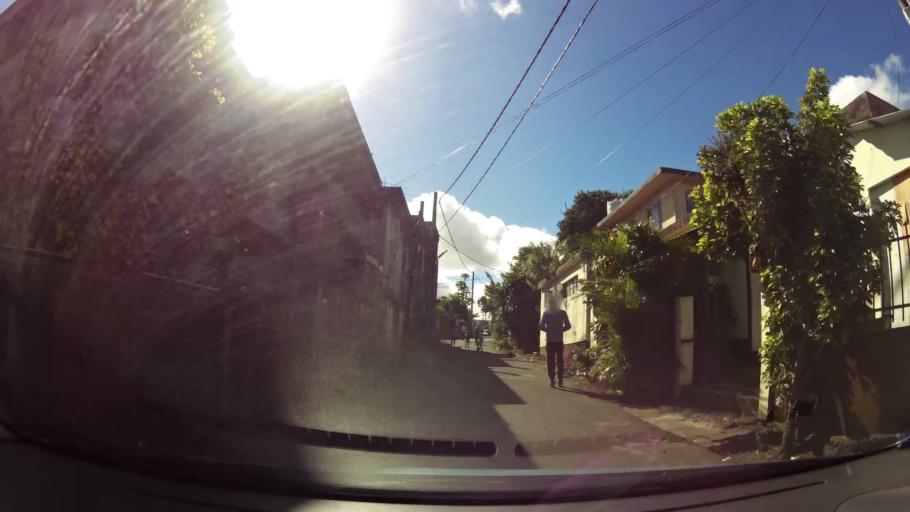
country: MU
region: Plaines Wilhems
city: Curepipe
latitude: -20.3032
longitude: 57.5033
